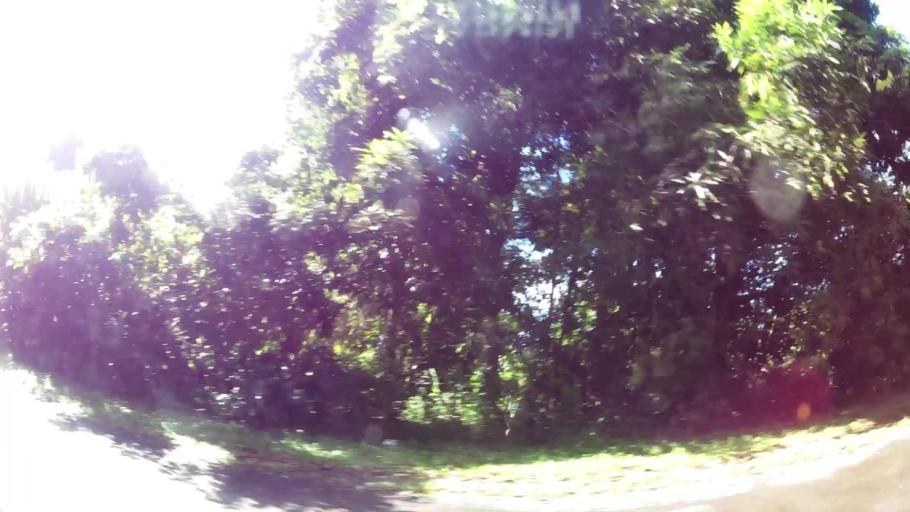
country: LC
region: Soufriere
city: Soufriere
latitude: 13.8743
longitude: -61.0425
